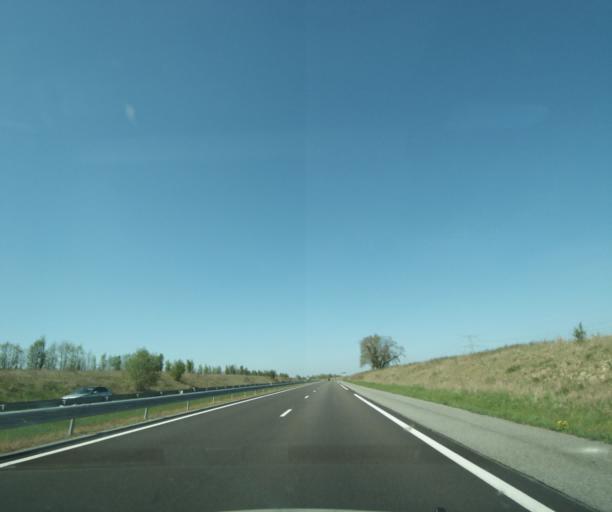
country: FR
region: Bourgogne
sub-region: Departement de la Nievre
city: Neuvy-sur-Loire
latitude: 47.5566
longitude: 2.8838
